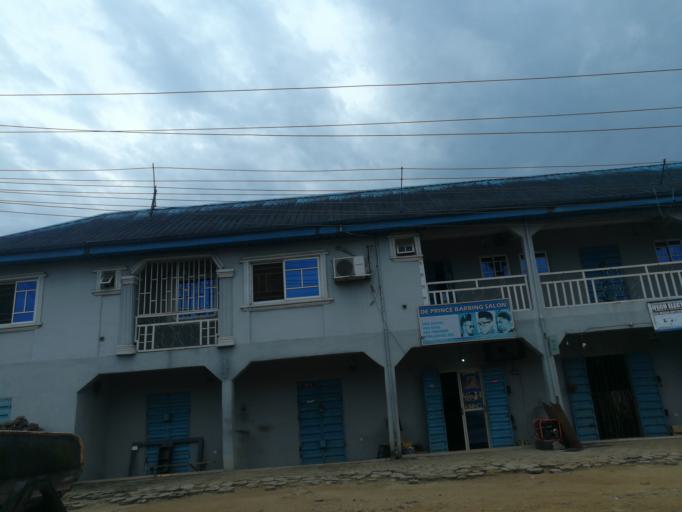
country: NG
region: Rivers
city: Port Harcourt
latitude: 4.7938
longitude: 6.9579
